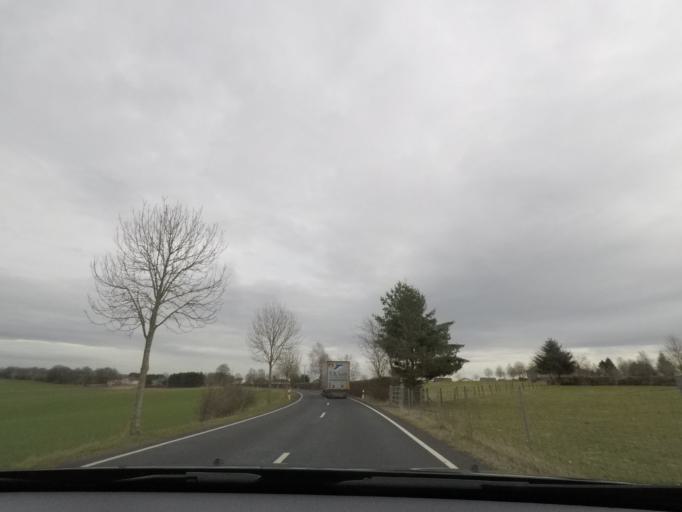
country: LU
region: Diekirch
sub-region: Canton de Wiltz
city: Winseler
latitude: 50.0119
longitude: 5.8780
